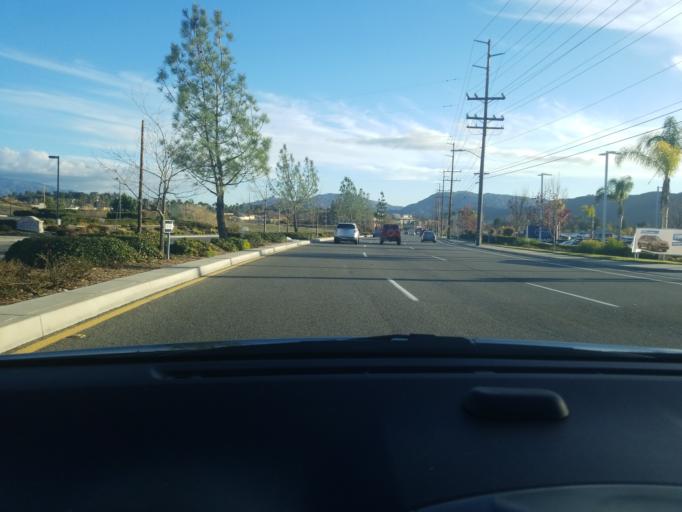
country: US
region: California
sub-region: Riverside County
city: Temecula
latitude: 33.5108
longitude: -117.1512
